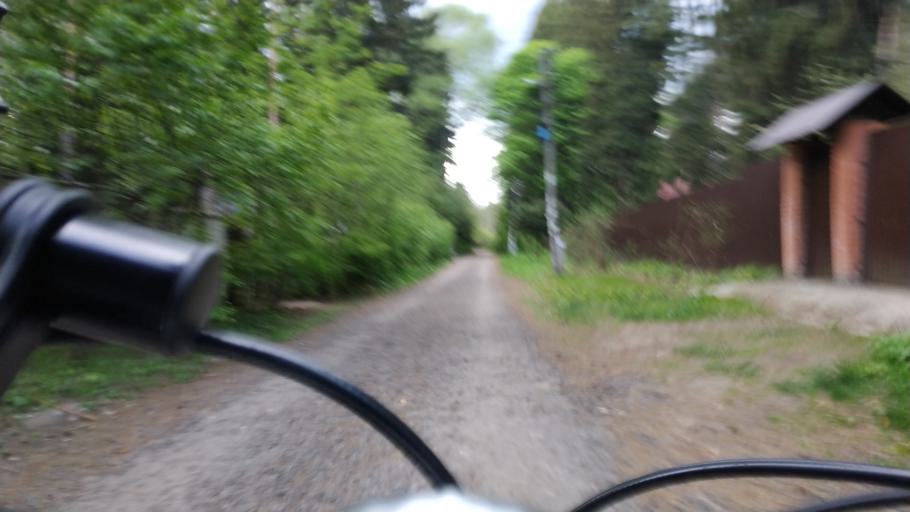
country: RU
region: Moskovskaya
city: Kratovo
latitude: 55.5830
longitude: 38.1739
